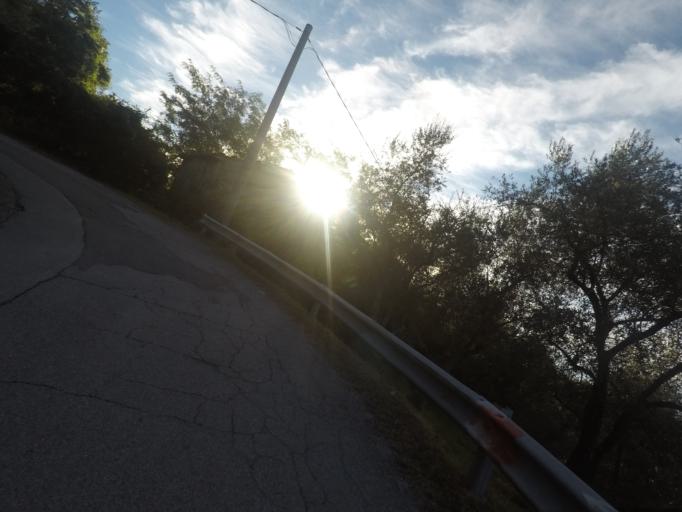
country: IT
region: Tuscany
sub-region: Provincia di Lucca
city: Stiava
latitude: 43.9172
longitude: 10.3698
